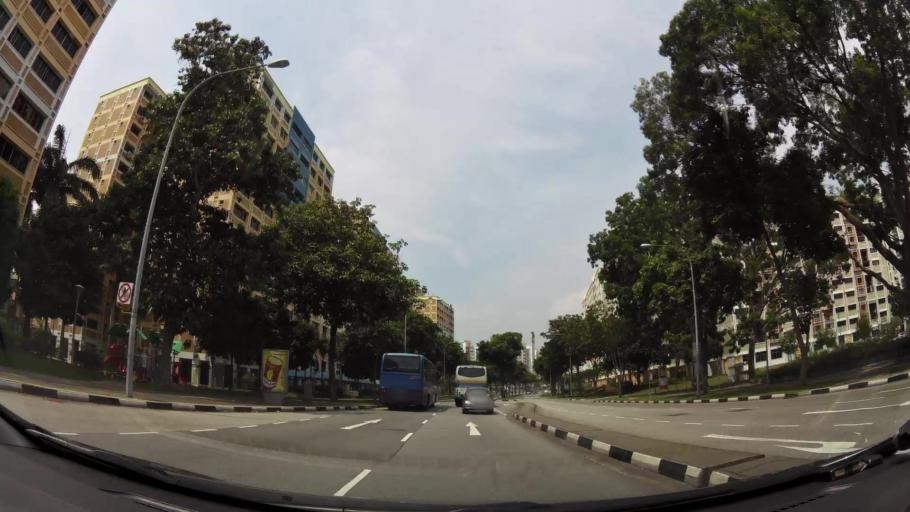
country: MY
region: Johor
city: Kampung Pasir Gudang Baru
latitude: 1.3696
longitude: 103.9512
